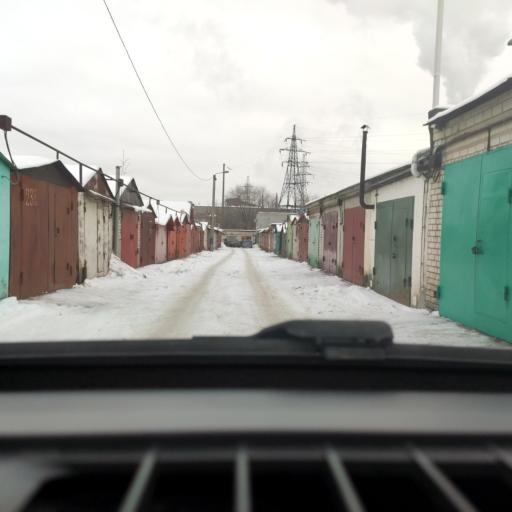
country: RU
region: Voronezj
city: Voronezh
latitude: 51.6884
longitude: 39.1462
